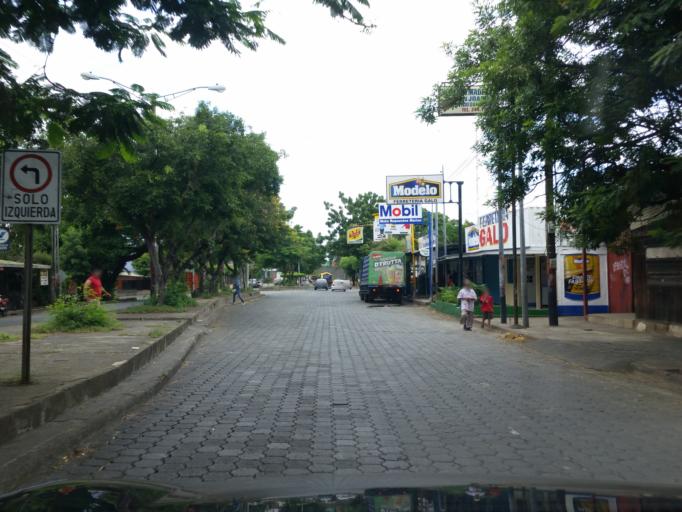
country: NI
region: Managua
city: Managua
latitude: 12.1480
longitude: -86.2238
